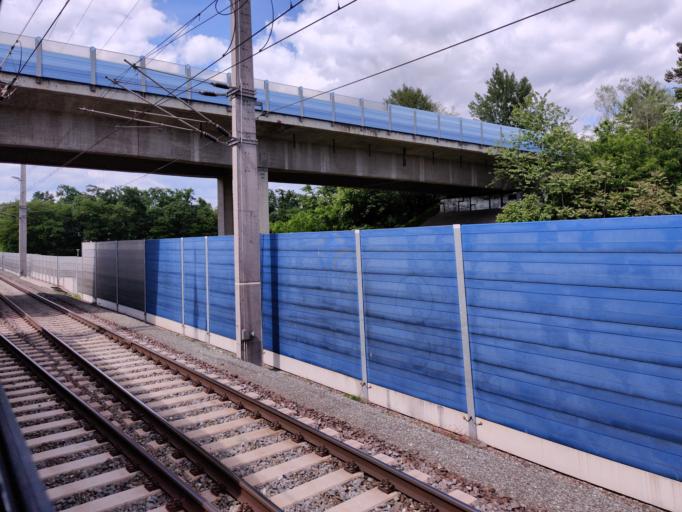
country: AT
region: Styria
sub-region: Politischer Bezirk Graz-Umgebung
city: Kalsdorf bei Graz
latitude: 46.9713
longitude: 15.4659
